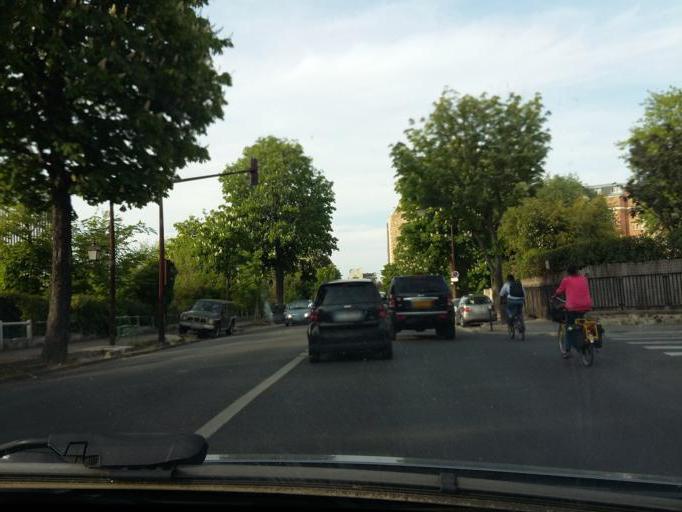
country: FR
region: Ile-de-France
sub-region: Departement des Hauts-de-Seine
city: Courbevoie
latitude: 48.8833
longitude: 2.2539
